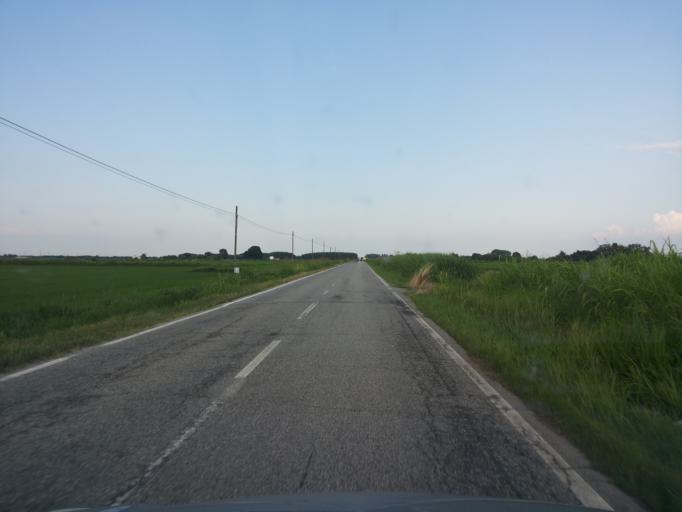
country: IT
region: Piedmont
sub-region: Provincia di Vercelli
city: Desana
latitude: 45.2656
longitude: 8.3810
